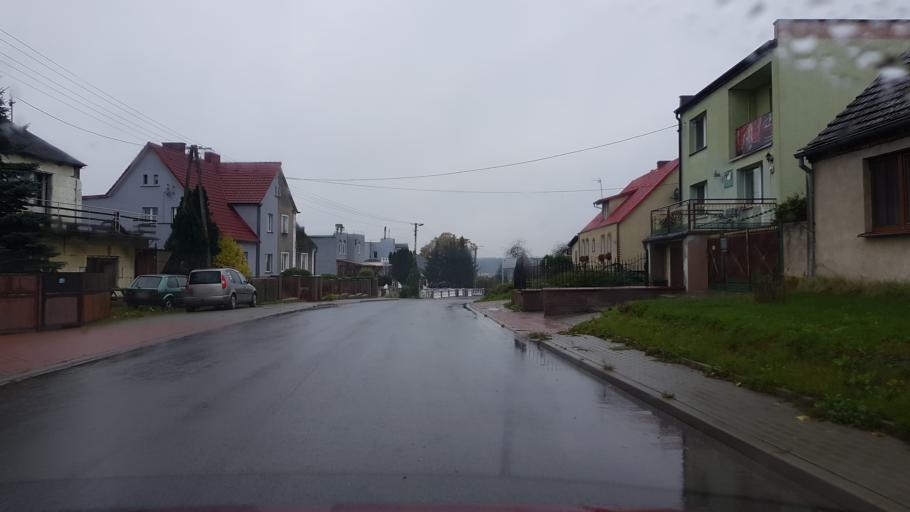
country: PL
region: Greater Poland Voivodeship
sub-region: Powiat zlotowski
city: Tarnowka
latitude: 53.3421
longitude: 16.8402
